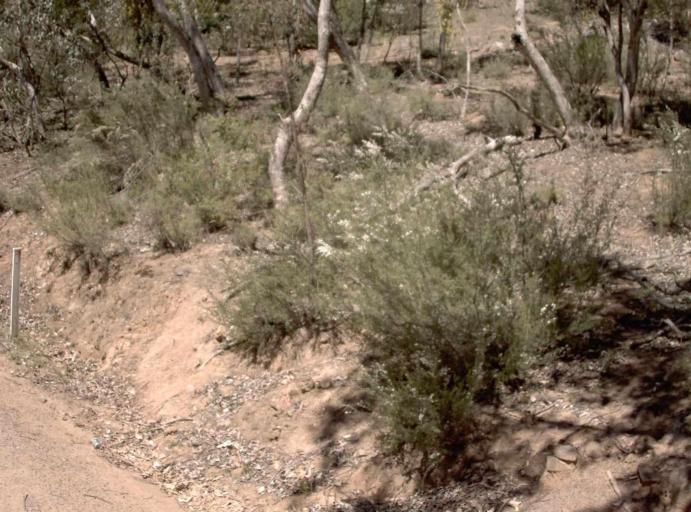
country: AU
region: New South Wales
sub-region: Snowy River
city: Jindabyne
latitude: -37.0637
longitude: 148.5163
